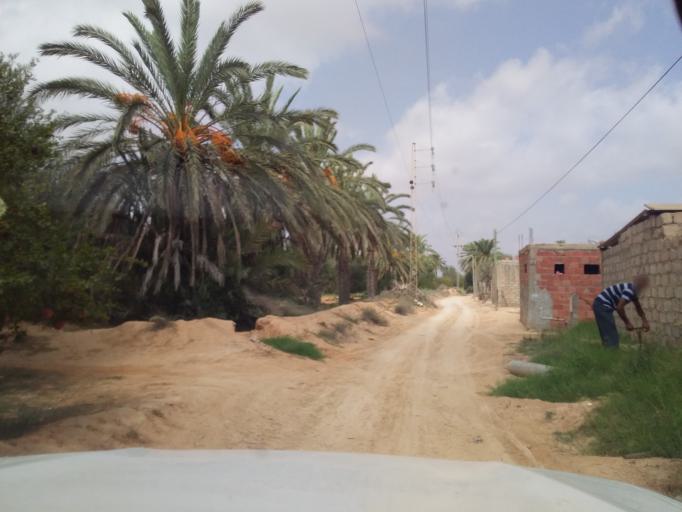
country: TN
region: Madanin
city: Medenine
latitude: 33.6248
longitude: 10.3115
